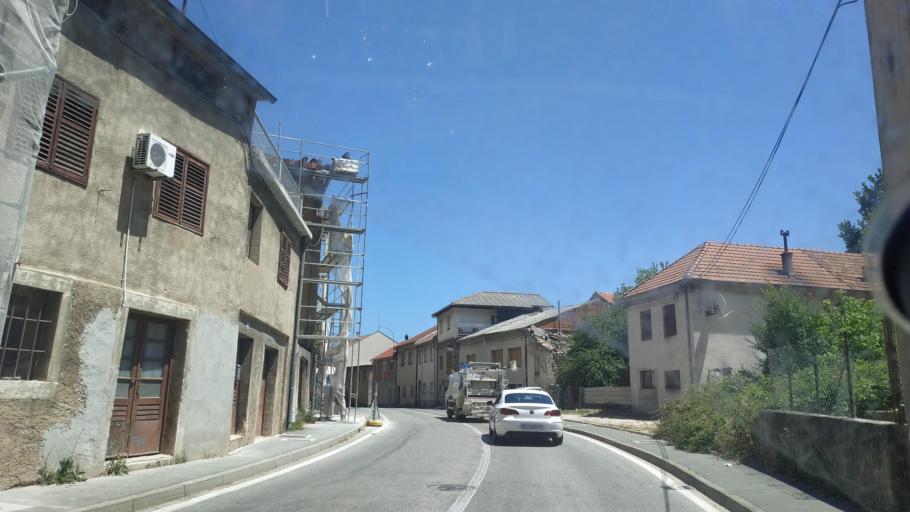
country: HR
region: Sibensko-Kniniska
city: Knin
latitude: 44.0318
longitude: 16.1922
